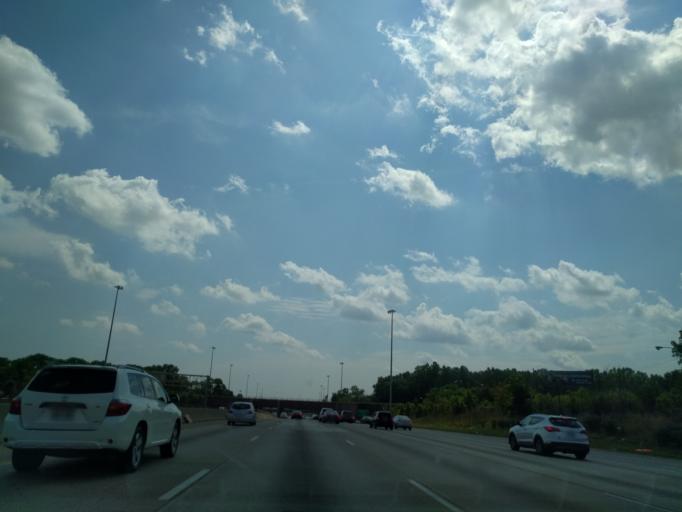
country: US
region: Illinois
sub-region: Cook County
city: Evergreen Park
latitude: 41.7329
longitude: -87.6249
